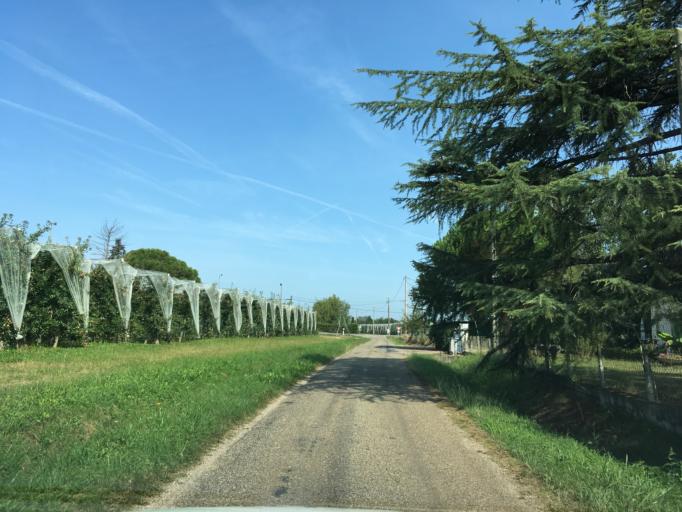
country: FR
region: Midi-Pyrenees
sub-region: Departement du Tarn-et-Garonne
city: Albias
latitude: 44.0658
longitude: 1.4181
